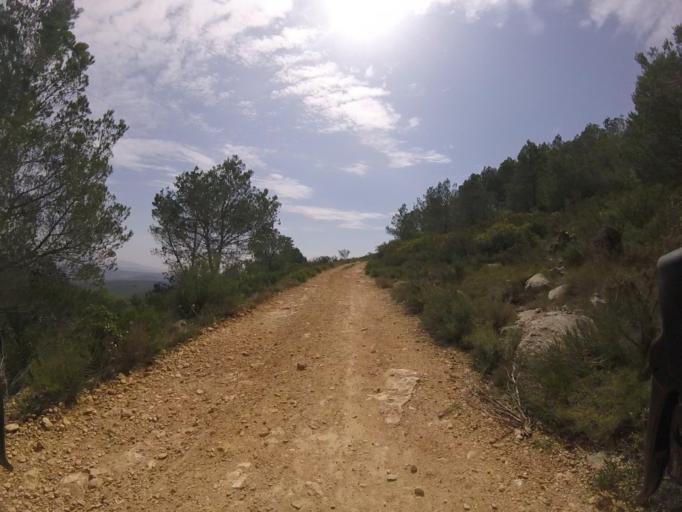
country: ES
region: Valencia
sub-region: Provincia de Castello
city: Cuevas de Vinroma
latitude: 40.2645
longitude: 0.1119
